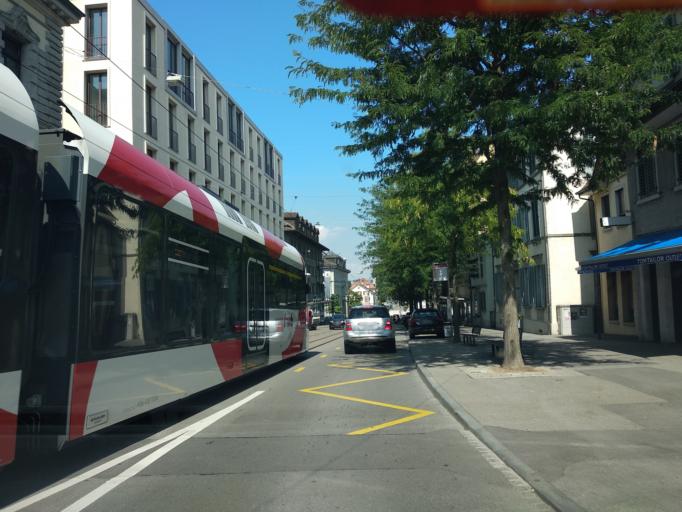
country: CH
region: Thurgau
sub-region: Frauenfeld District
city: Frauenfeld
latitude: 47.5557
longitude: 8.8965
